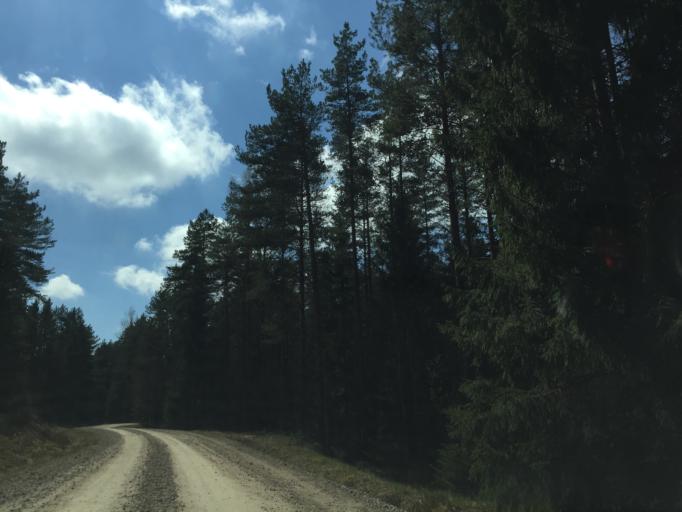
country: EE
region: Valgamaa
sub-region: Valga linn
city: Valga
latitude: 57.5962
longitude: 26.1318
